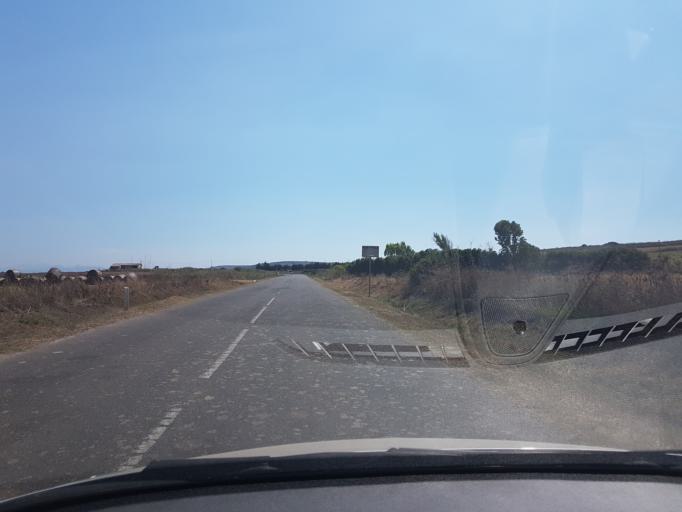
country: IT
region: Sardinia
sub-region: Provincia di Oristano
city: Nurachi
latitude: 39.9831
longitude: 8.4546
